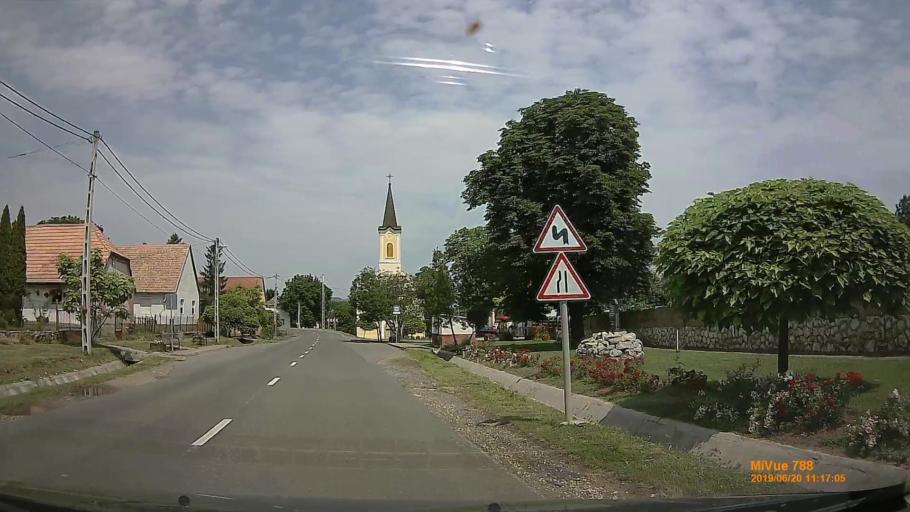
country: HU
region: Baranya
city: Pecsvarad
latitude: 46.1564
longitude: 18.4736
